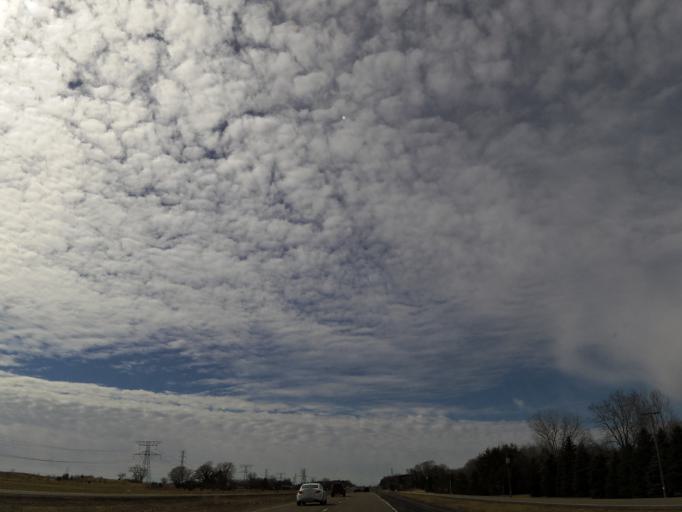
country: US
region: Minnesota
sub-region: Washington County
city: Lake Elmo
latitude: 45.0359
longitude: -92.8948
